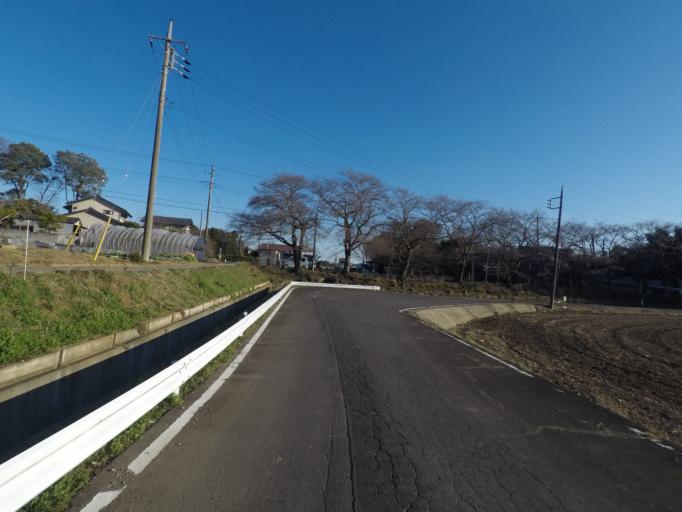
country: JP
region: Ibaraki
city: Ishige
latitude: 36.1411
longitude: 140.0076
